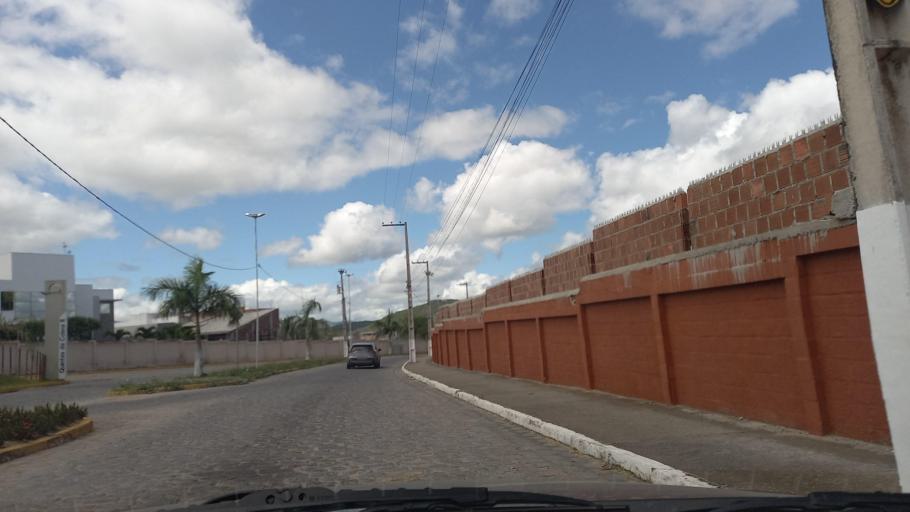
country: BR
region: Pernambuco
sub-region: Caruaru
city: Caruaru
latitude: -8.2503
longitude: -35.9501
